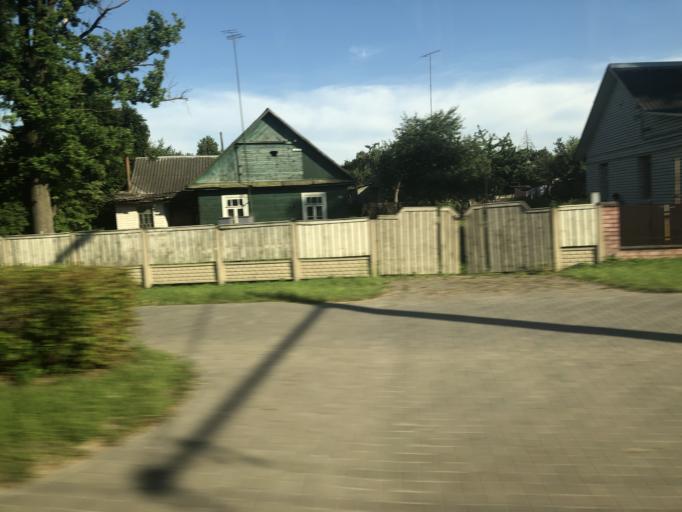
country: BY
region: Grodnenskaya
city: Hrodna
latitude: 53.6567
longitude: 23.8034
